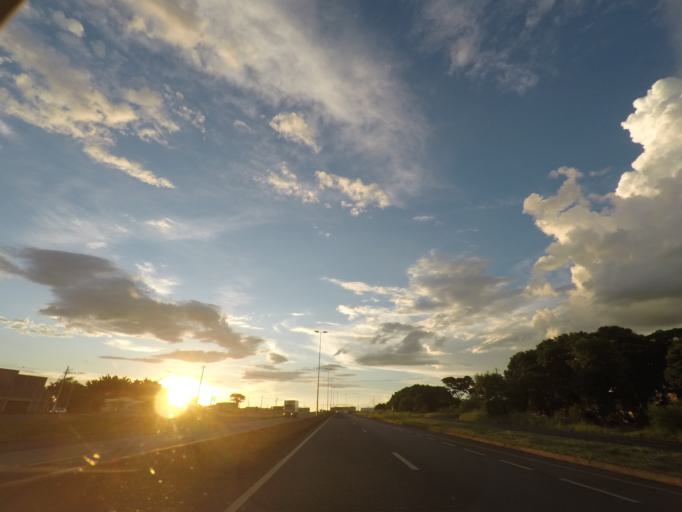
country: BR
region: Minas Gerais
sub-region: Uberaba
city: Uberaba
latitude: -19.7793
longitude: -47.9654
